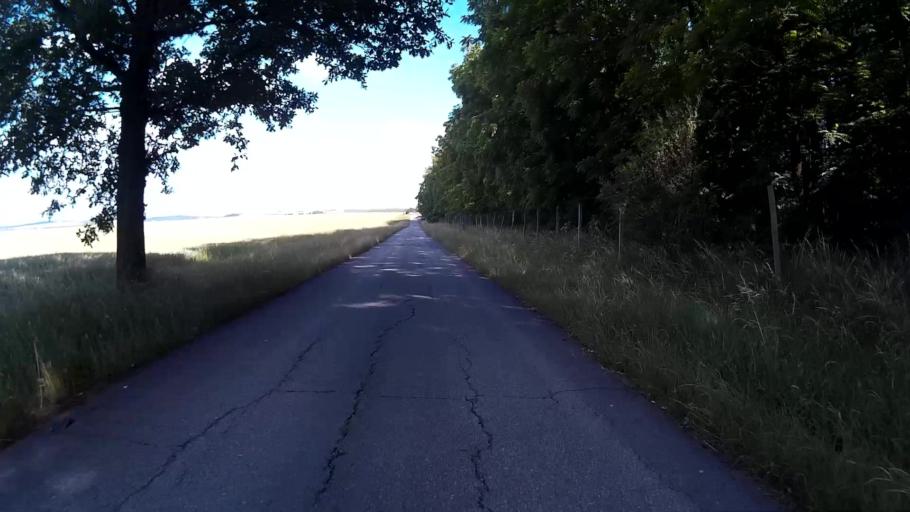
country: CZ
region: South Moravian
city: Menin
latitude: 49.0469
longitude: 16.7003
